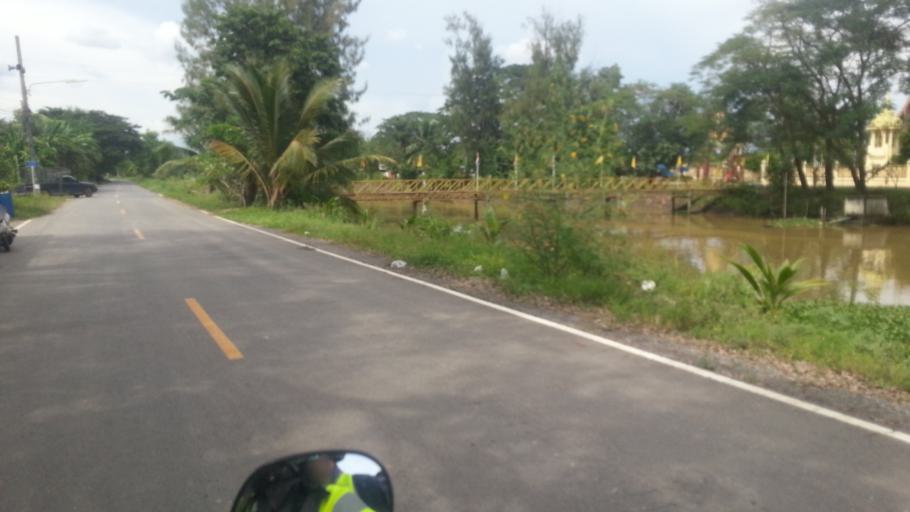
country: TH
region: Pathum Thani
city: Nong Suea
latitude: 14.0751
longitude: 100.8238
